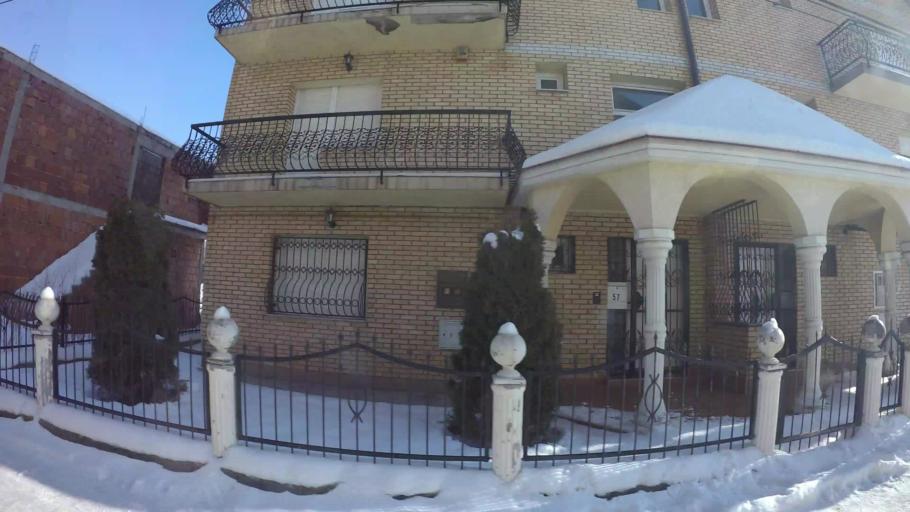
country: BA
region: Federation of Bosnia and Herzegovina
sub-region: Kanton Sarajevo
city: Sarajevo
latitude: 43.8138
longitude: 18.3247
